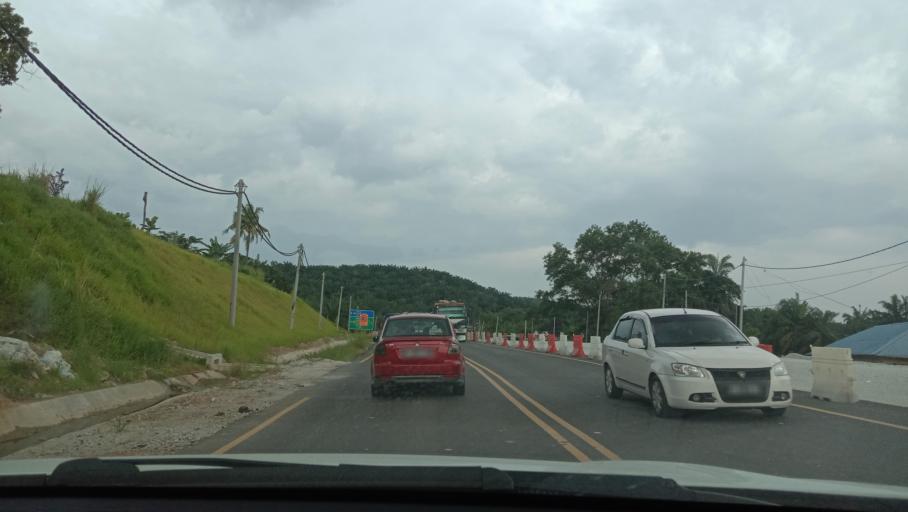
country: MY
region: Selangor
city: Batu Arang
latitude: 3.2628
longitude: 101.4595
